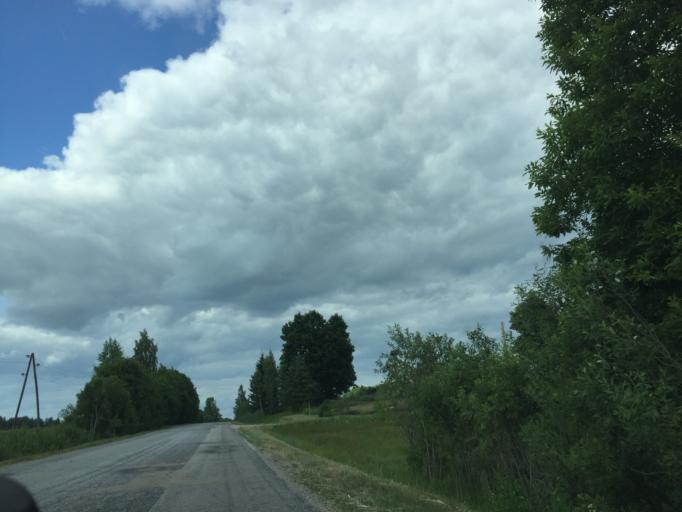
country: LV
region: Skriveri
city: Skriveri
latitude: 56.8184
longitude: 25.1188
